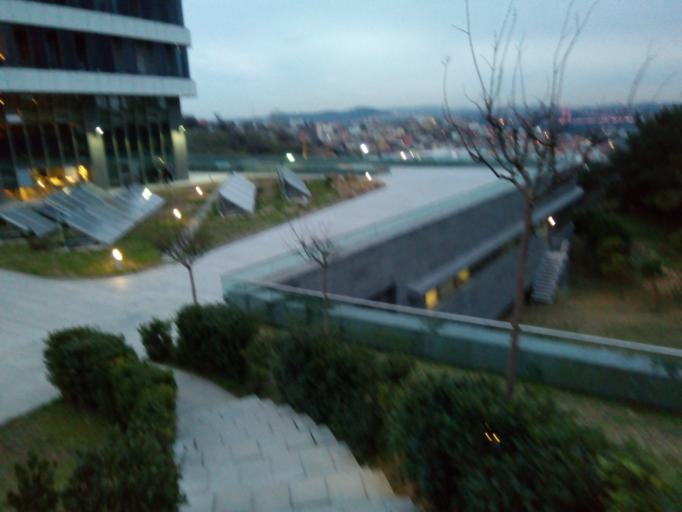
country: TR
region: Istanbul
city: Sisli
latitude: 41.1074
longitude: 29.0316
